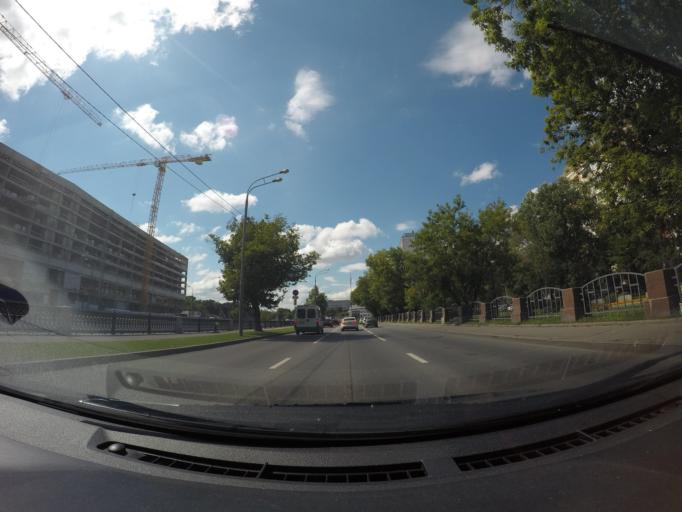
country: RU
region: Moscow
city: Lefortovo
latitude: 55.7730
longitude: 37.6955
